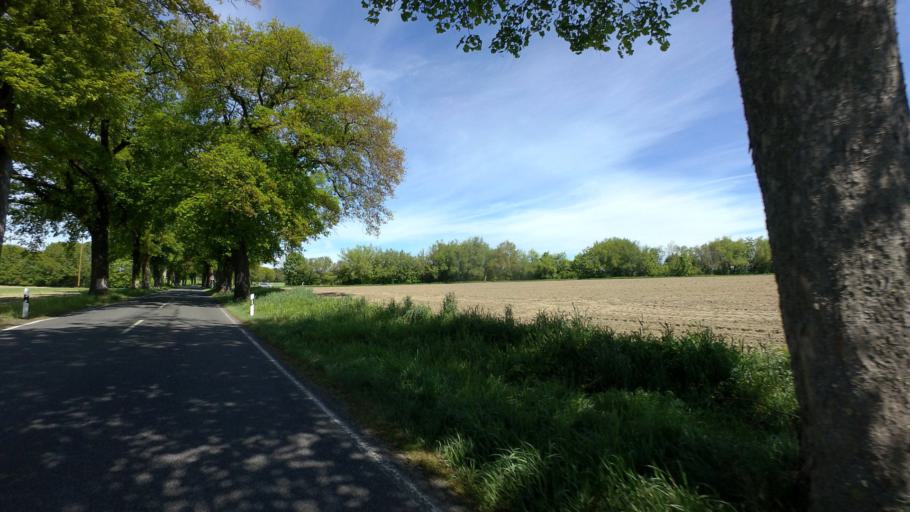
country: DE
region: Brandenburg
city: Michendorf
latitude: 52.2522
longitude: 13.0804
